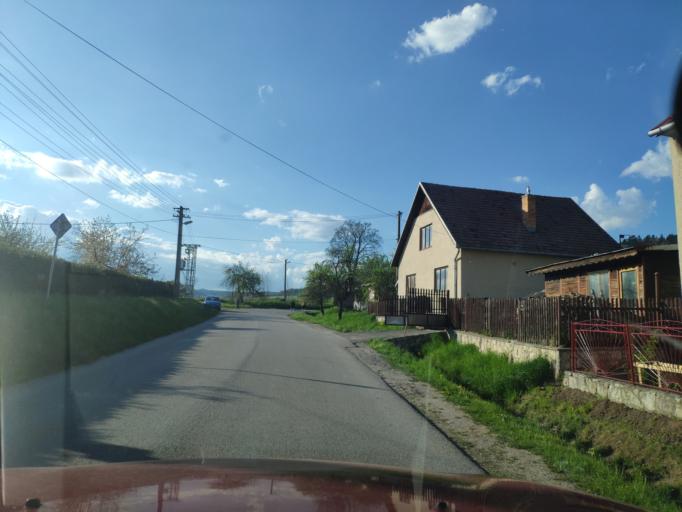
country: SK
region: Presovsky
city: Spisske Podhradie
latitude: 49.0264
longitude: 20.7974
